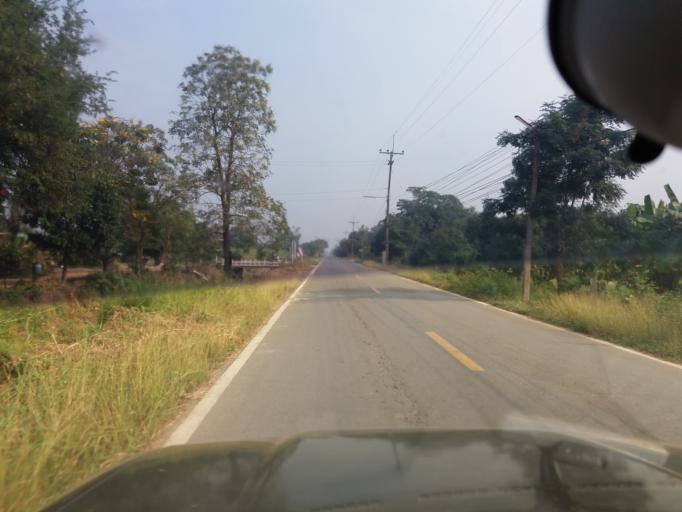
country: TH
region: Suphan Buri
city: Doem Bang Nang Buat
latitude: 14.8773
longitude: 100.1765
